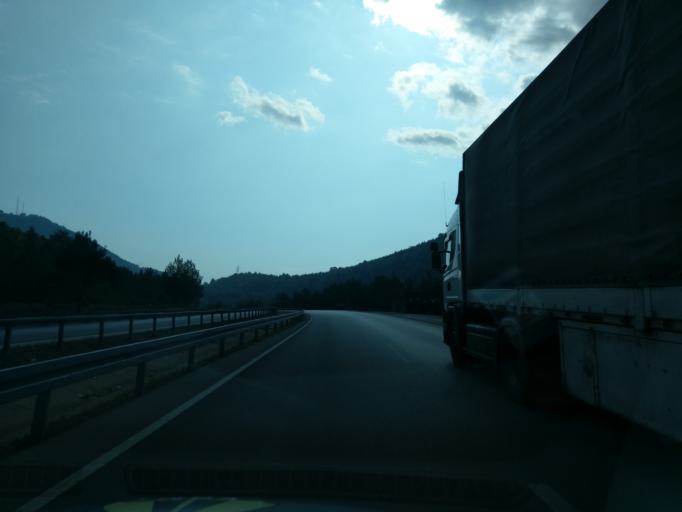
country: TR
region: Amasya
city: Akdag
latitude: 40.7525
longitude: 36.0748
